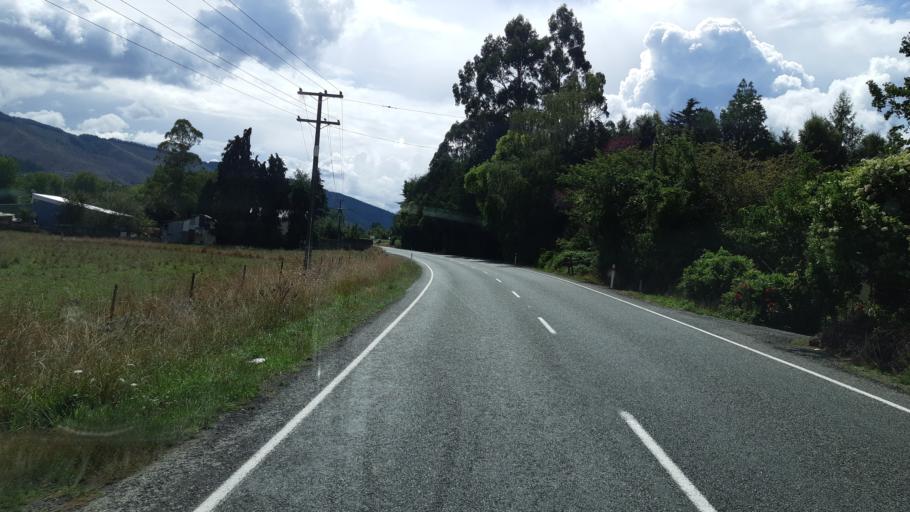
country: NZ
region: Tasman
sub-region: Tasman District
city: Wakefield
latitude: -41.4742
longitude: 172.8053
